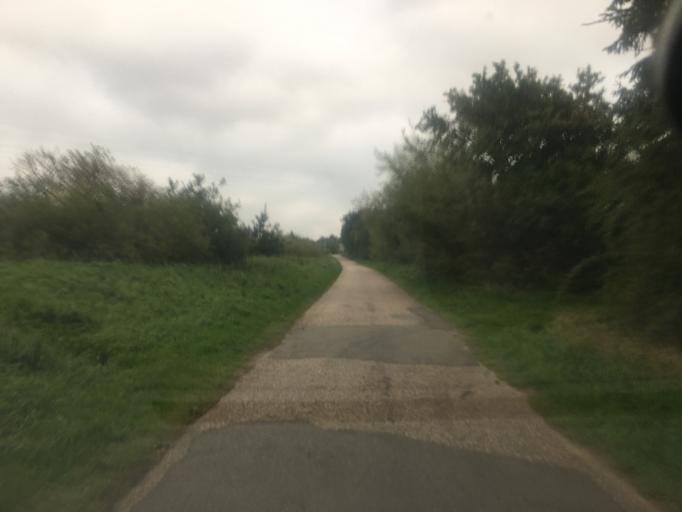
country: DE
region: Schleswig-Holstein
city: Ellhoft
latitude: 54.9435
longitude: 8.9601
